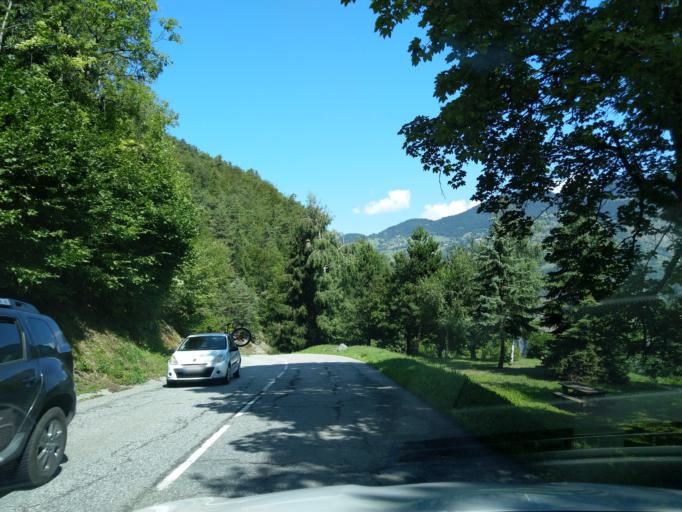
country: FR
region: Rhone-Alpes
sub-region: Departement de la Savoie
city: Les Allues
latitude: 45.4418
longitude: 6.5596
